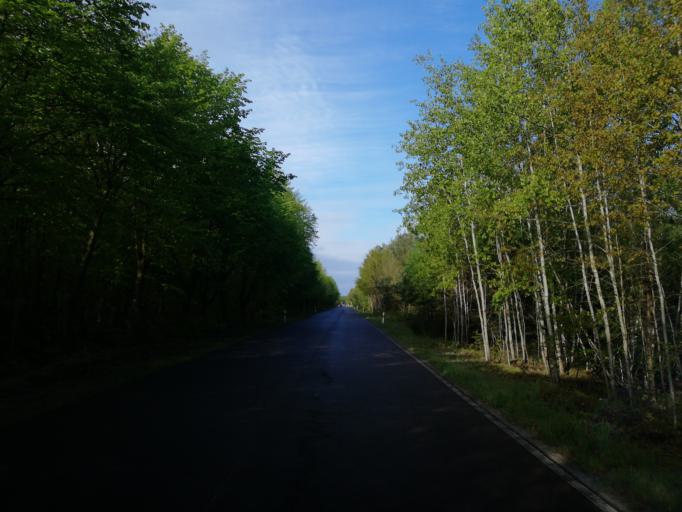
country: DE
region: Brandenburg
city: Lauchhammer
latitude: 51.5192
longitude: 13.7614
